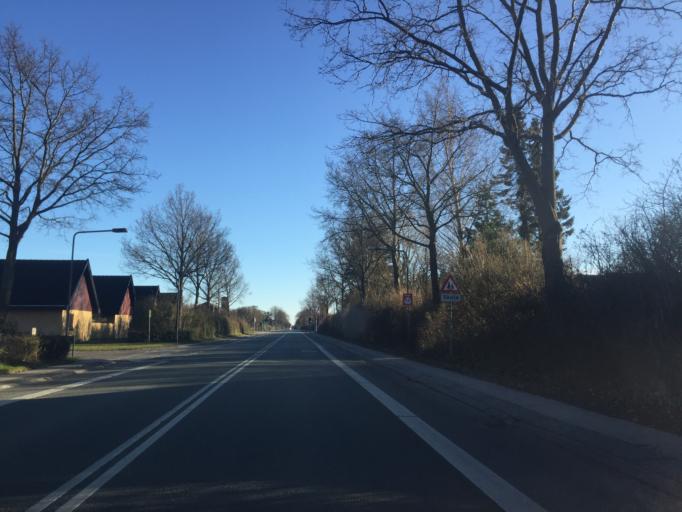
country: DK
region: Capital Region
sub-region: Dragor Kommune
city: Dragor
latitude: 55.6007
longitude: 12.6587
